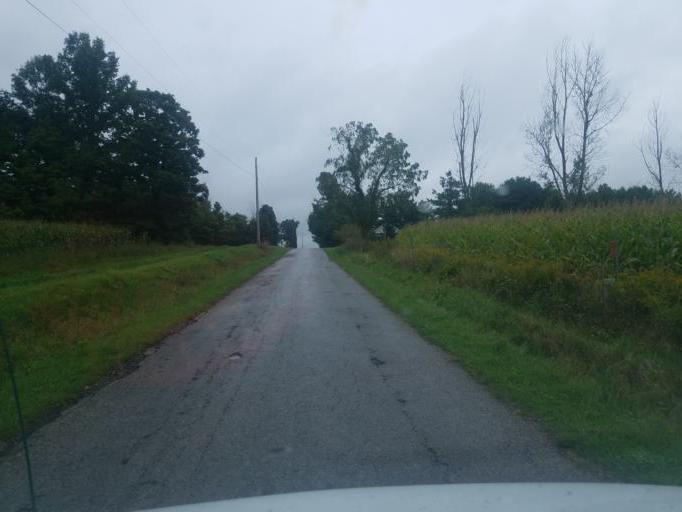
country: US
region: Ohio
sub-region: Wayne County
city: West Salem
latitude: 40.9378
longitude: -82.1378
